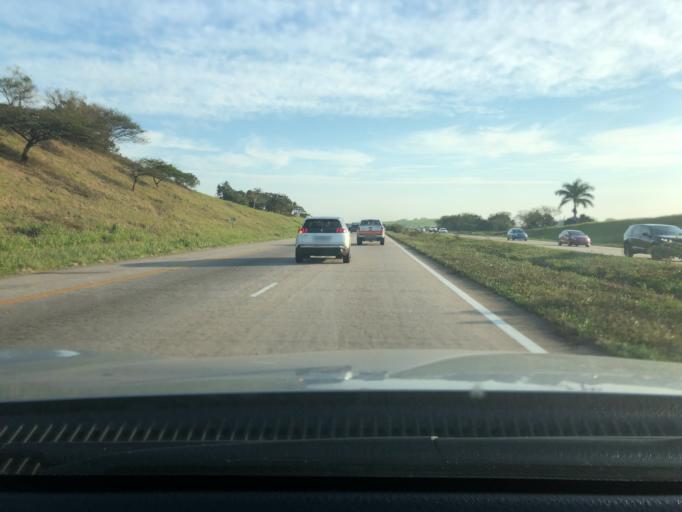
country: ZA
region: KwaZulu-Natal
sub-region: iLembe District Municipality
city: Ballitoville
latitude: -29.5749
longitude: 31.1503
